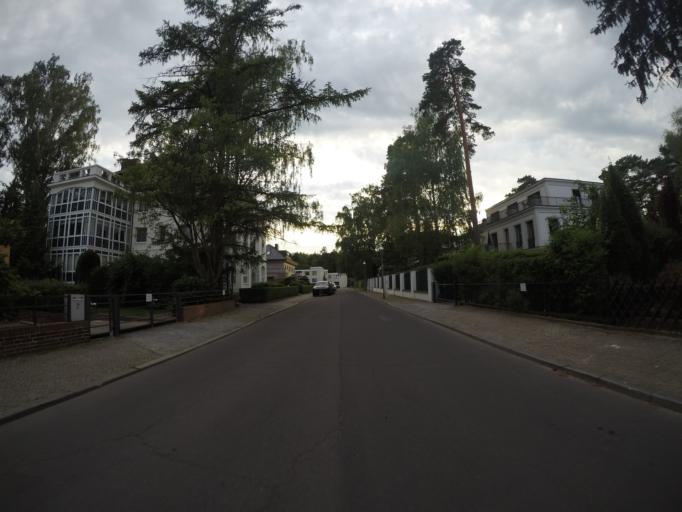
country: DE
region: Berlin
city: Dahlem
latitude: 52.4694
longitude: 13.2750
